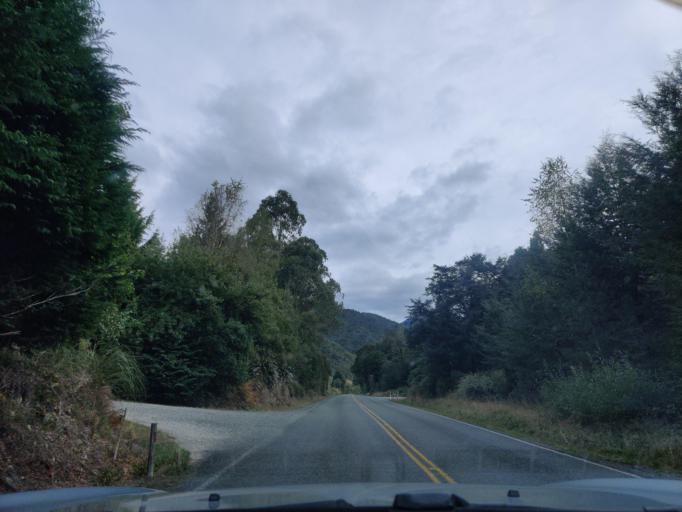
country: NZ
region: Tasman
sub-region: Tasman District
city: Wakefield
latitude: -41.7244
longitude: 172.4081
